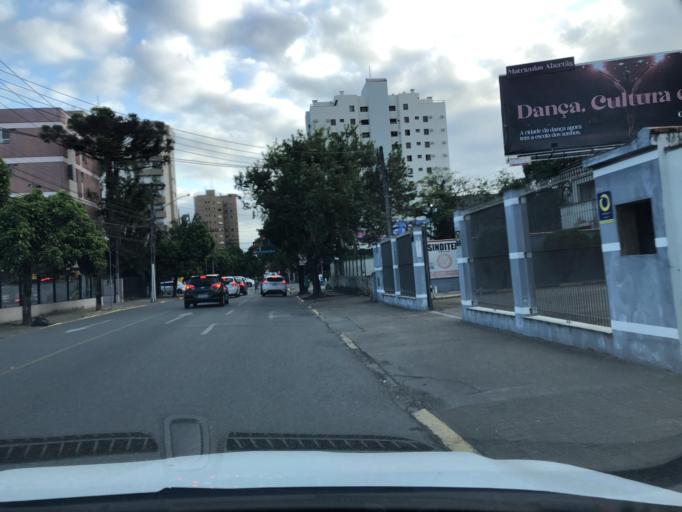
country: BR
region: Santa Catarina
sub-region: Joinville
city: Joinville
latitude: -26.2943
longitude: -48.8457
